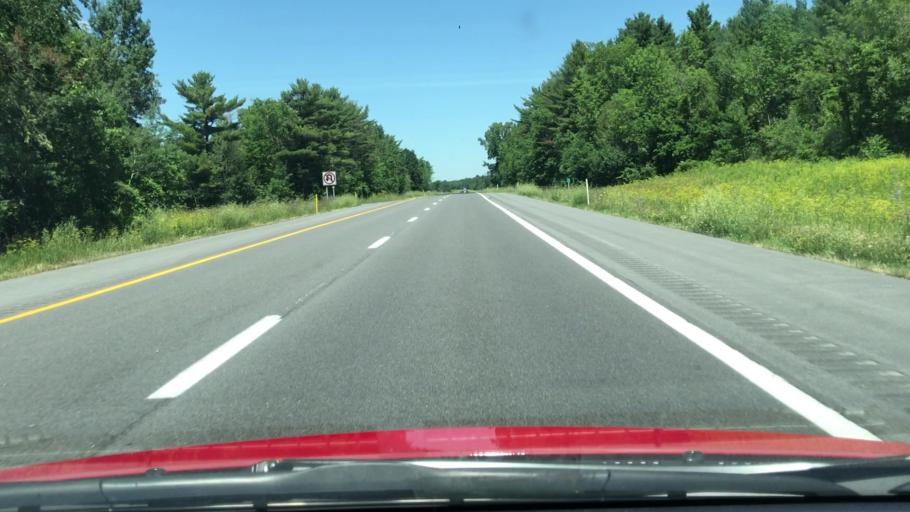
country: US
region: New York
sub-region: Clinton County
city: Cumberland Head
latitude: 44.8273
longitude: -73.4464
